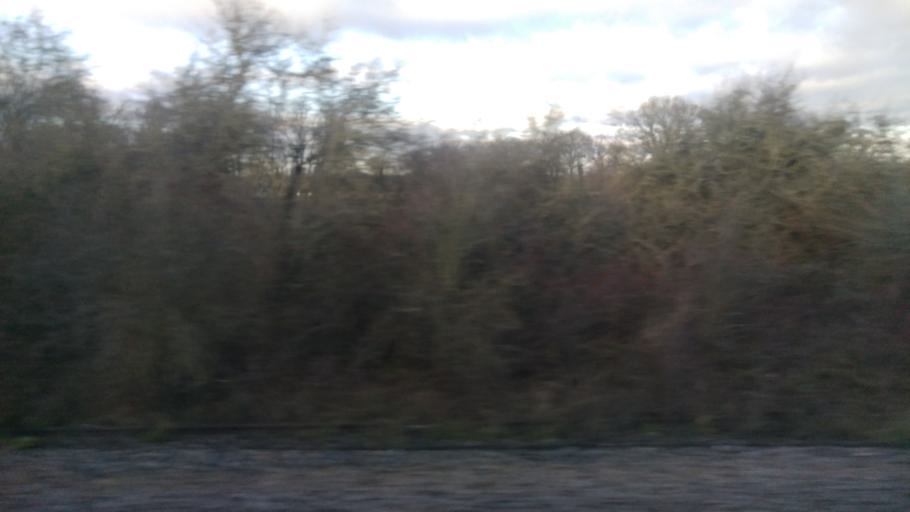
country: GB
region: England
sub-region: Kent
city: Headcorn
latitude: 51.1681
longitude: 0.5961
